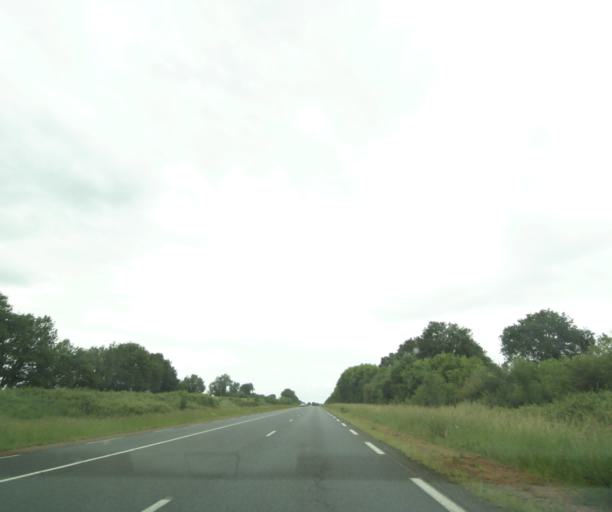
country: FR
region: Poitou-Charentes
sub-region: Departement des Deux-Sevres
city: Airvault
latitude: 46.8015
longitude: -0.2124
